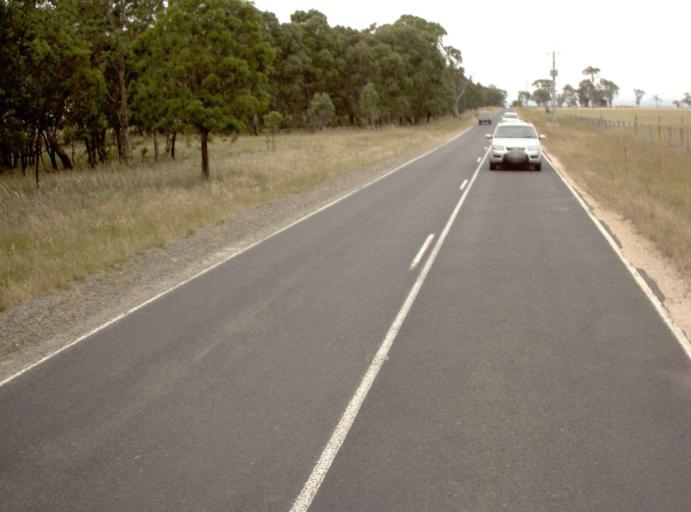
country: AU
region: Victoria
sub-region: Wellington
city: Heyfield
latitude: -38.0399
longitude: 146.7670
